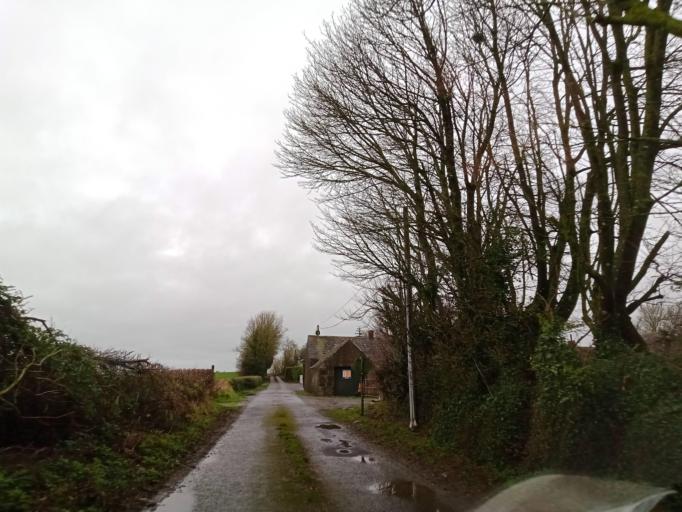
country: IE
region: Munster
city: Fethard
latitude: 52.5597
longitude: -7.7096
